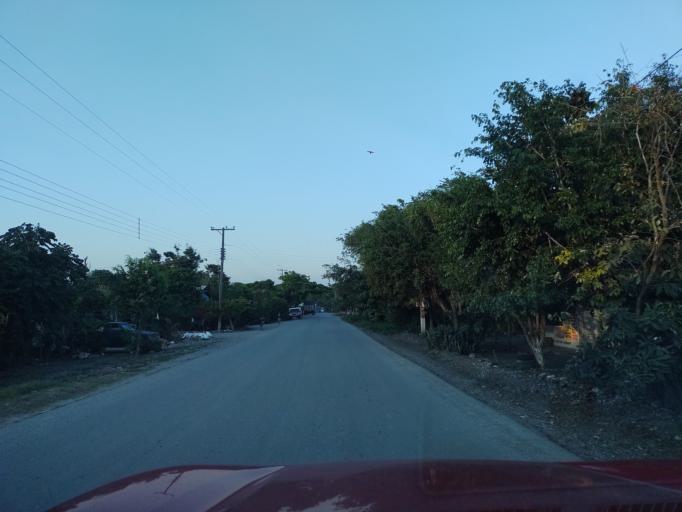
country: MX
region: Veracruz
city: Agua Dulce
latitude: 20.3166
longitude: -97.2714
